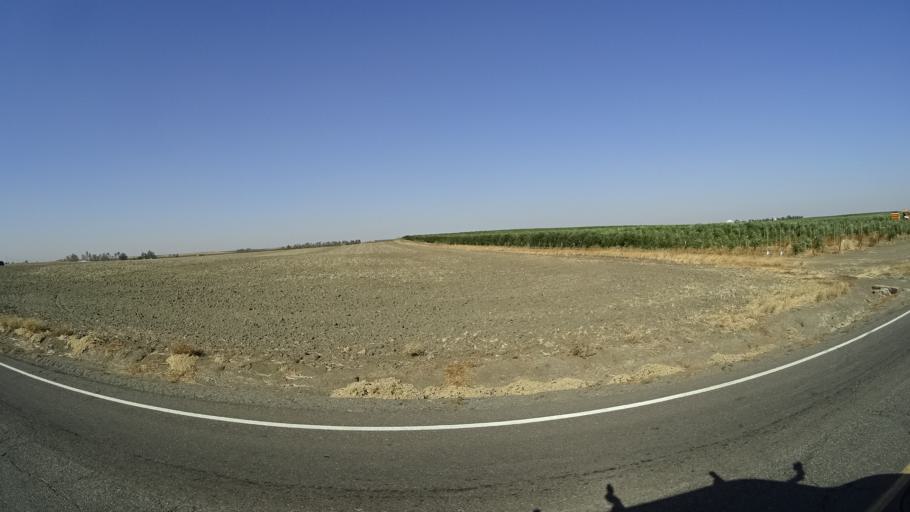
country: US
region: California
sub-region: Yolo County
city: Cottonwood
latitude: 38.7133
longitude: -121.9156
